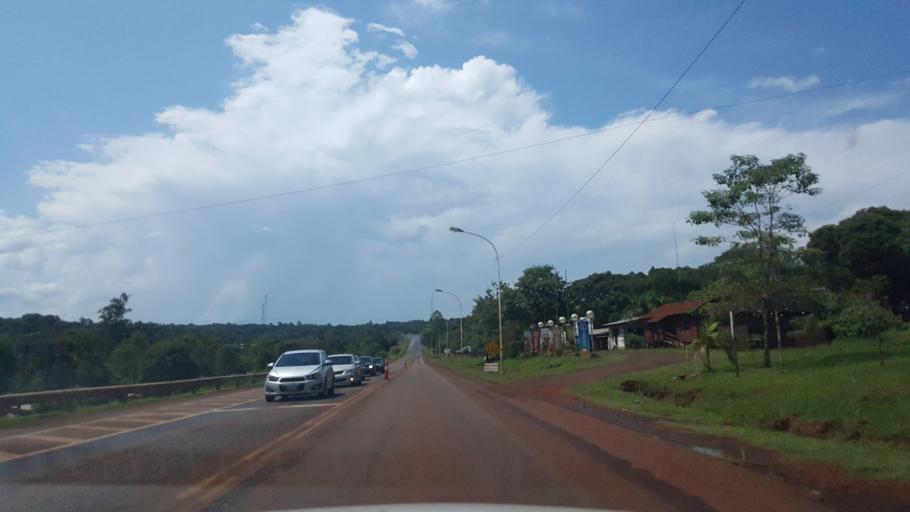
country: AR
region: Misiones
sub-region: Departamento de Eldorado
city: Eldorado
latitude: -26.4151
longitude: -54.6419
